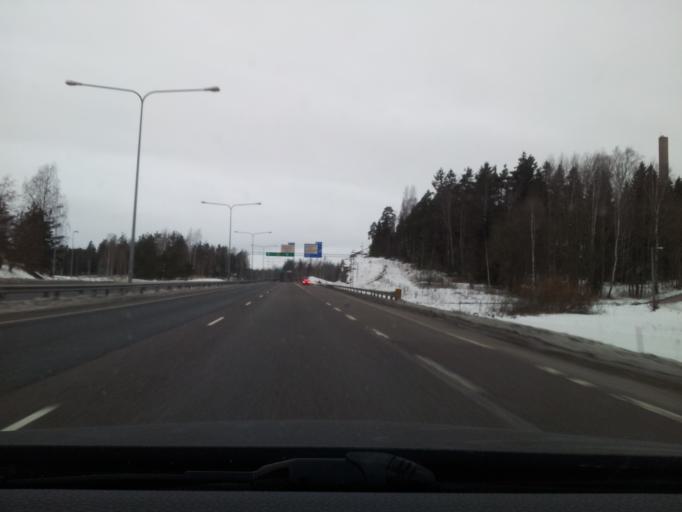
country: FI
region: Uusimaa
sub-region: Helsinki
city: Espoo
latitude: 60.1574
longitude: 24.6336
